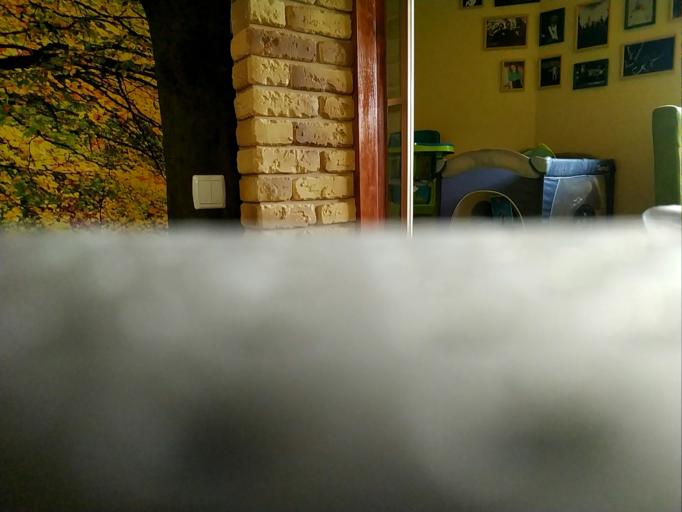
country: RU
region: Kaluga
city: Seredeyskiy
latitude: 53.9524
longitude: 35.3355
